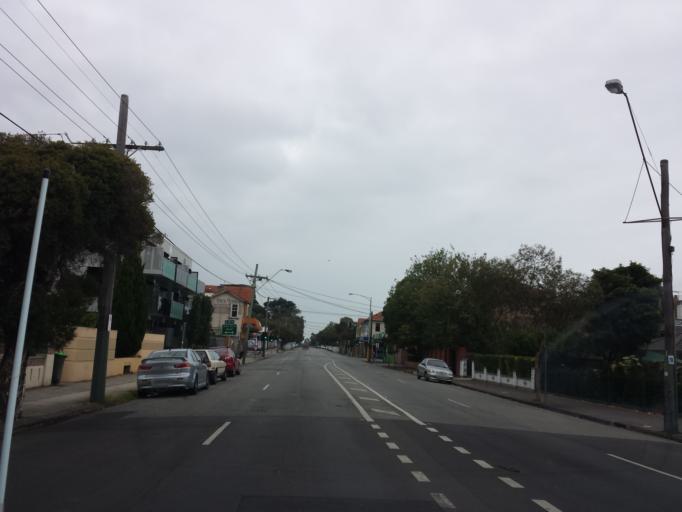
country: AU
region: Victoria
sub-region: Port Phillip
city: Balaclava
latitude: -37.8759
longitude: 144.9982
